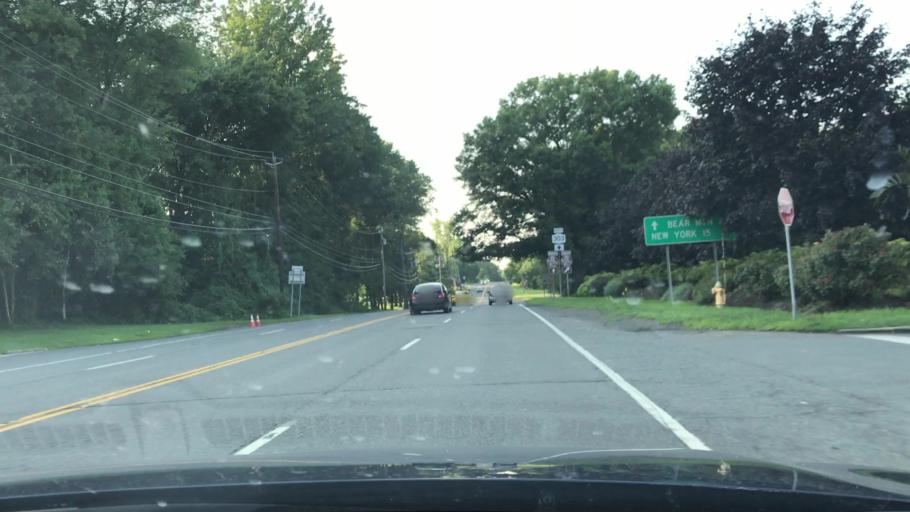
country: US
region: New York
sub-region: Rockland County
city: Tappan
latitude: 41.0319
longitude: -73.9448
